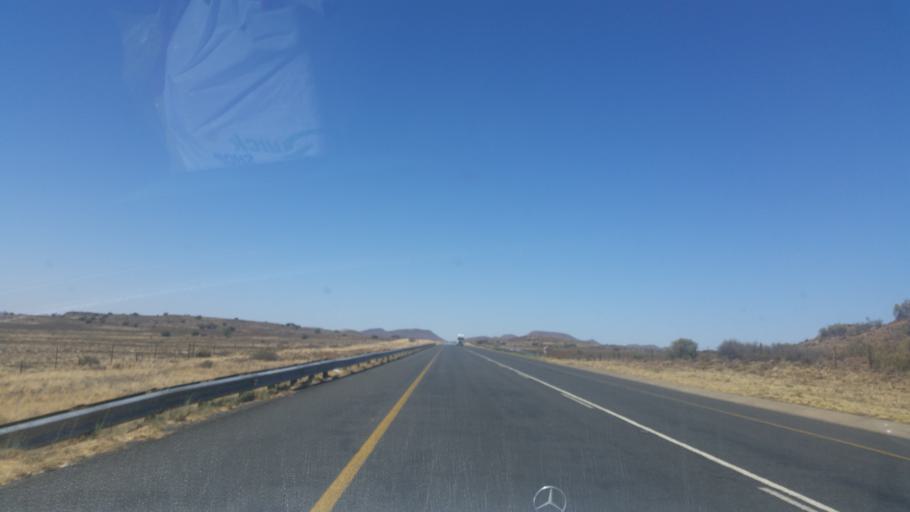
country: ZA
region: Northern Cape
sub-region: Pixley ka Seme District Municipality
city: Colesberg
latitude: -30.6174
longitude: 25.3072
